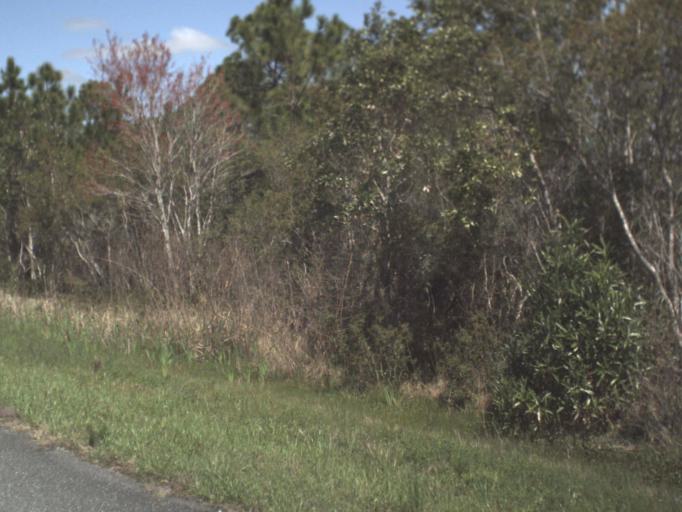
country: US
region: Florida
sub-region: Wakulla County
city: Crawfordville
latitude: 29.9945
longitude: -84.3968
